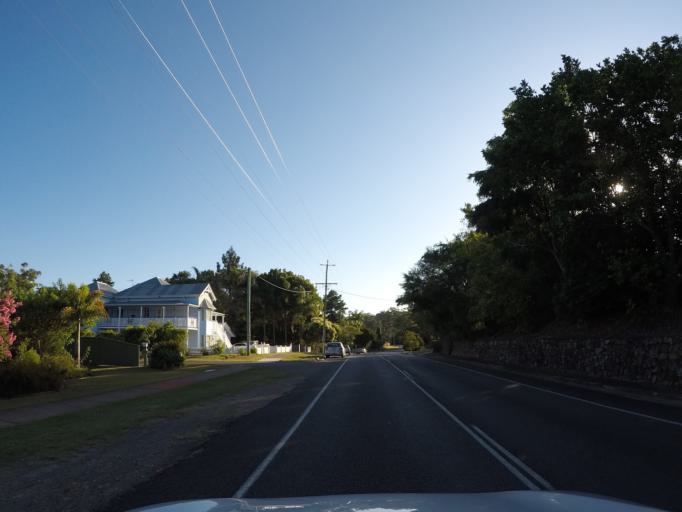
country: AU
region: Queensland
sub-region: Sunshine Coast
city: Nambour
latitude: -26.6260
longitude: 152.8636
